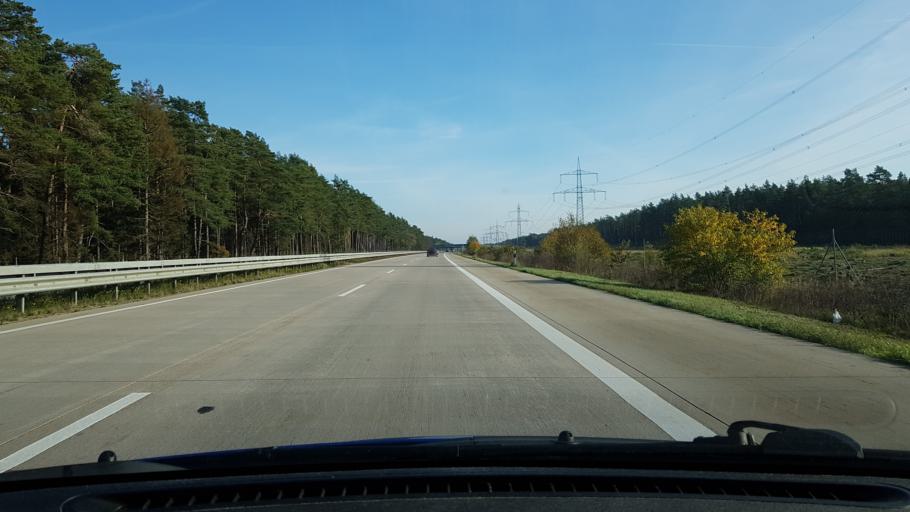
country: DE
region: Schleswig-Holstein
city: Gudow
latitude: 53.5293
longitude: 10.7695
